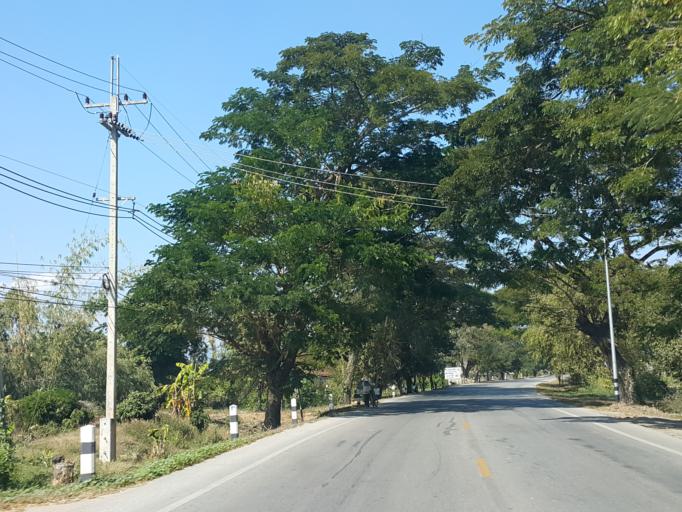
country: TH
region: Chiang Mai
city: Mae Taeng
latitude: 19.0504
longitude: 98.9621
